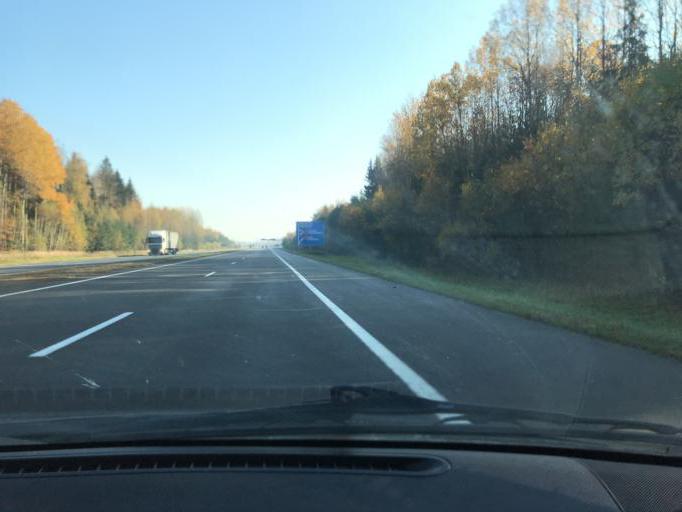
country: BY
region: Minsk
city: Bobr
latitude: 54.3716
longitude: 29.2716
